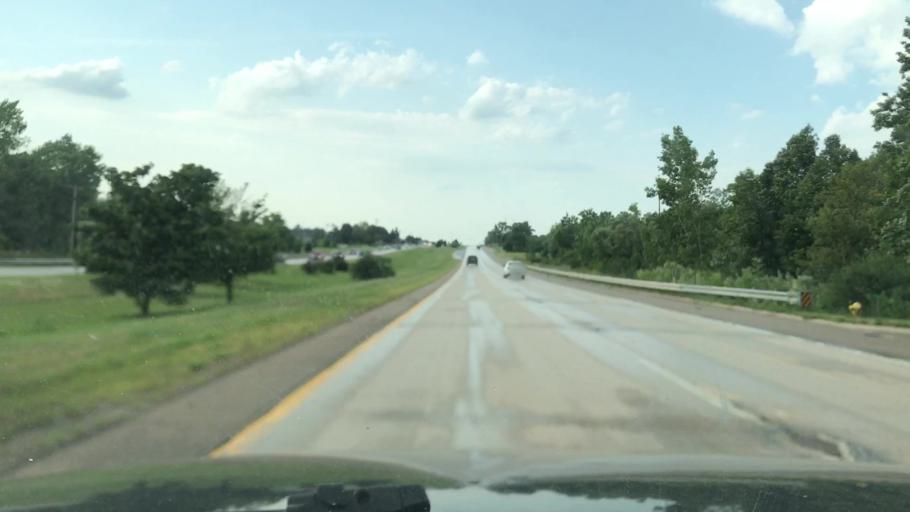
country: US
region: Michigan
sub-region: Kent County
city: East Grand Rapids
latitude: 42.8714
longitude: -85.5554
